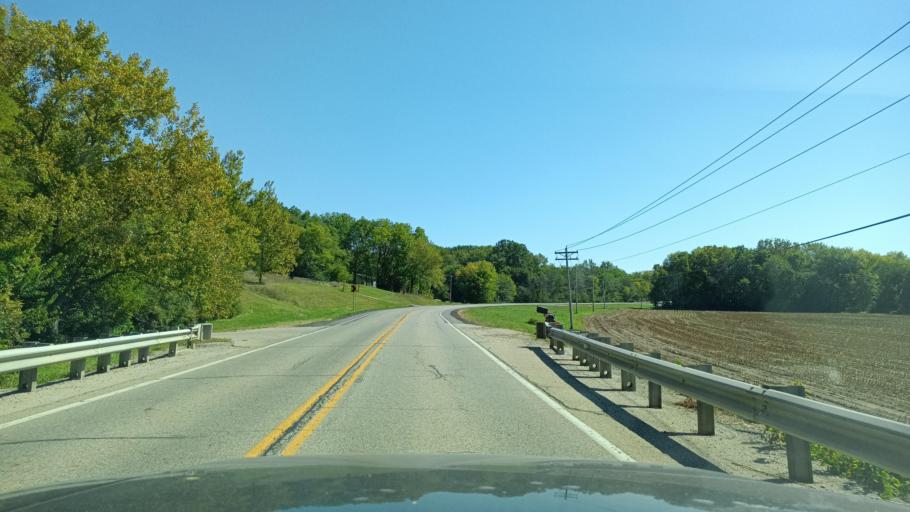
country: US
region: Illinois
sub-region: Woodford County
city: Eureka
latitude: 40.6262
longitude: -89.2457
